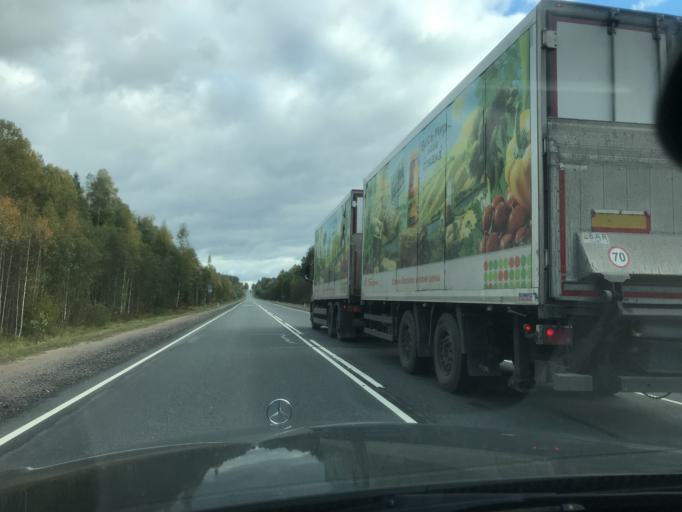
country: RU
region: Pskov
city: Idritsa
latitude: 56.5789
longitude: 28.8877
